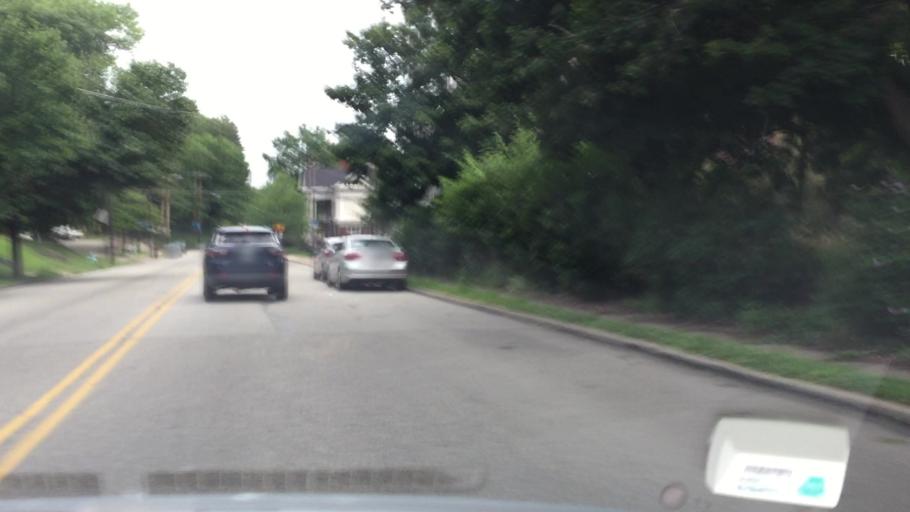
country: US
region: Pennsylvania
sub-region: Allegheny County
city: Pittsburgh
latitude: 40.4684
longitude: -80.0099
